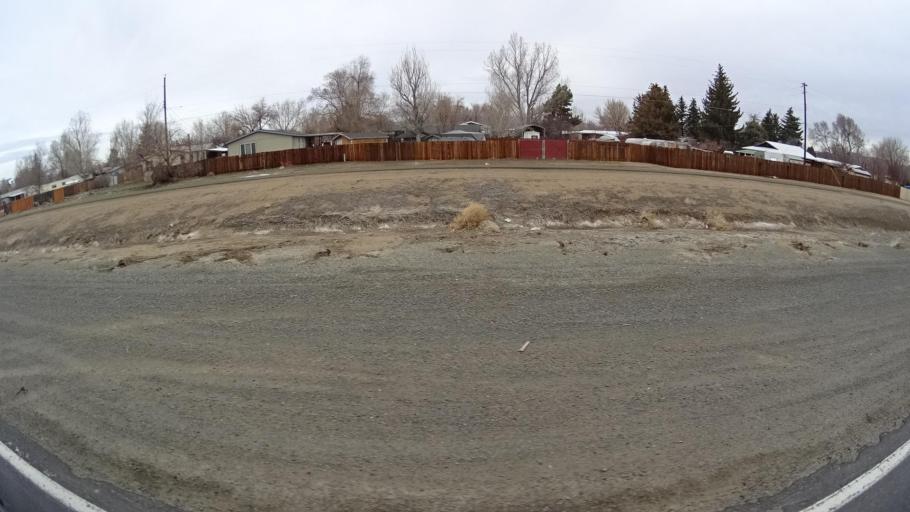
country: US
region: Nevada
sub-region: Washoe County
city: Lemmon Valley
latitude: 39.6420
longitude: -119.8371
